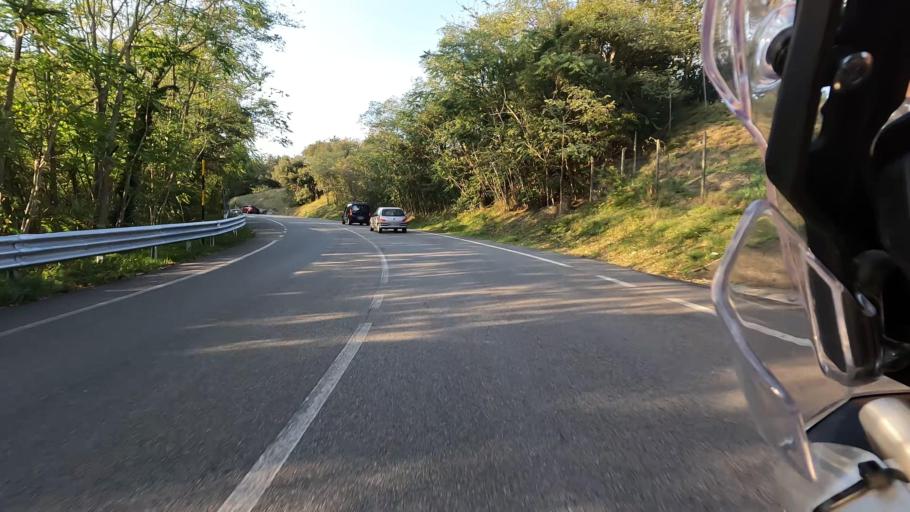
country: IT
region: Liguria
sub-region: Provincia di Savona
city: Osteria dei Cacciatori-Stella
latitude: 44.4246
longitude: 8.4753
